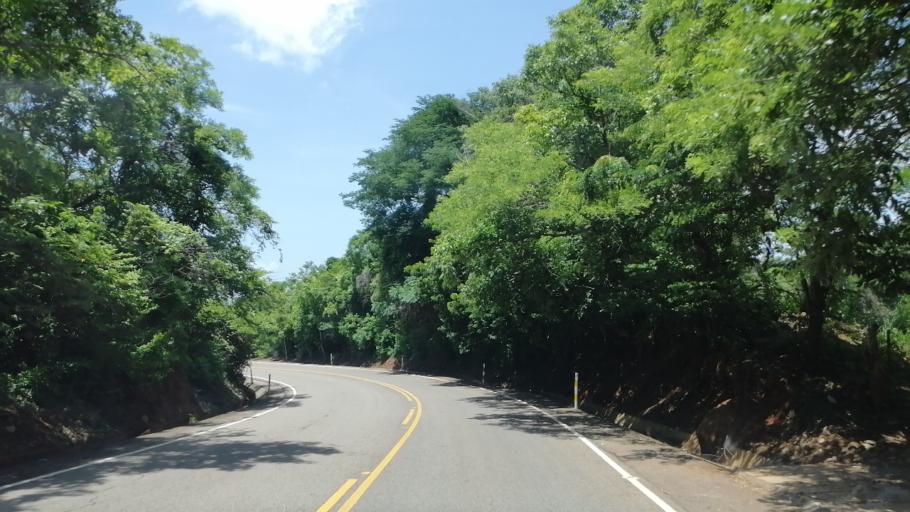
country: SV
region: Chalatenango
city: Nueva Concepcion
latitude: 14.1720
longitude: -89.3139
